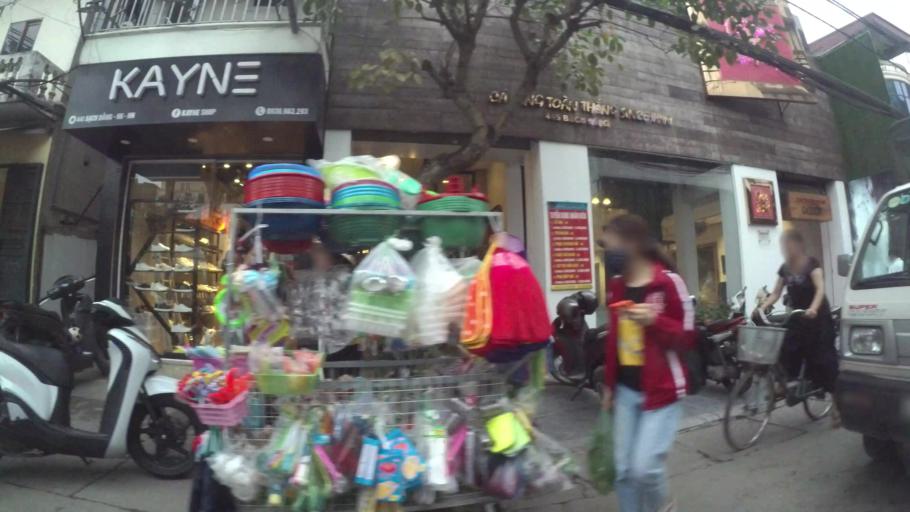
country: VN
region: Ha Noi
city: Hoan Kiem
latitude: 21.0251
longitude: 105.8620
